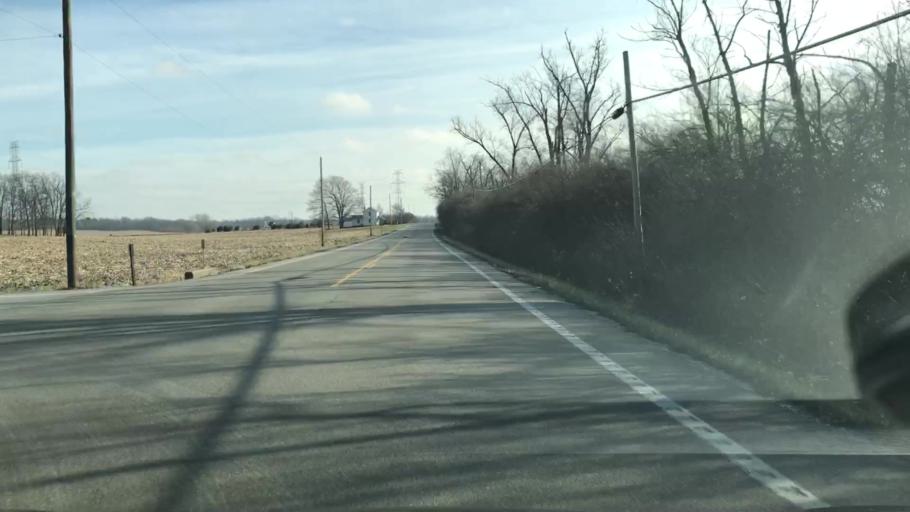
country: US
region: Ohio
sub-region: Greene County
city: Fairborn
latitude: 39.8089
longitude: -83.9784
